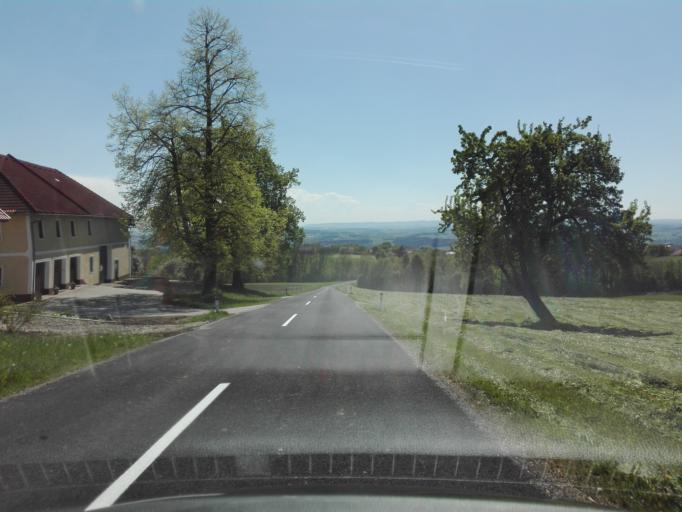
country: AT
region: Upper Austria
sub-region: Politischer Bezirk Rohrbach
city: Kleinzell im Muehlkreis
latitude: 48.3628
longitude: 13.9194
